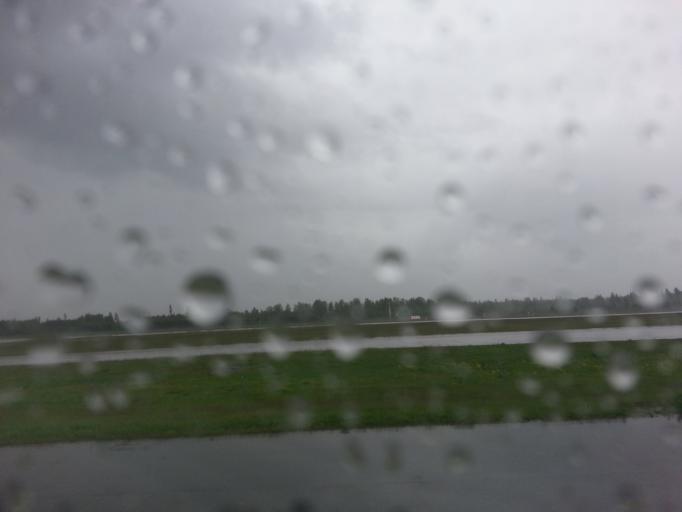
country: NO
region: Akershus
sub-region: Ullensaker
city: Jessheim
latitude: 60.1996
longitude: 11.1161
